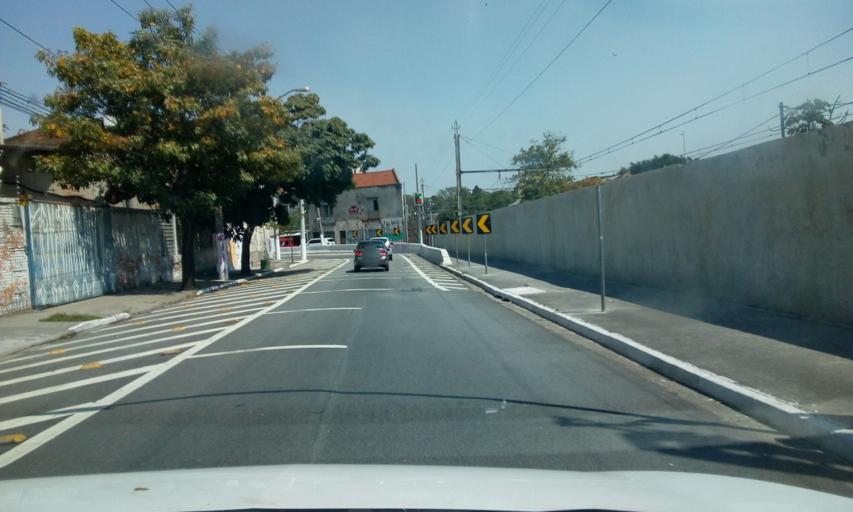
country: BR
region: Sao Paulo
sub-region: Sao Paulo
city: Sao Paulo
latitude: -23.5188
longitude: -46.7092
